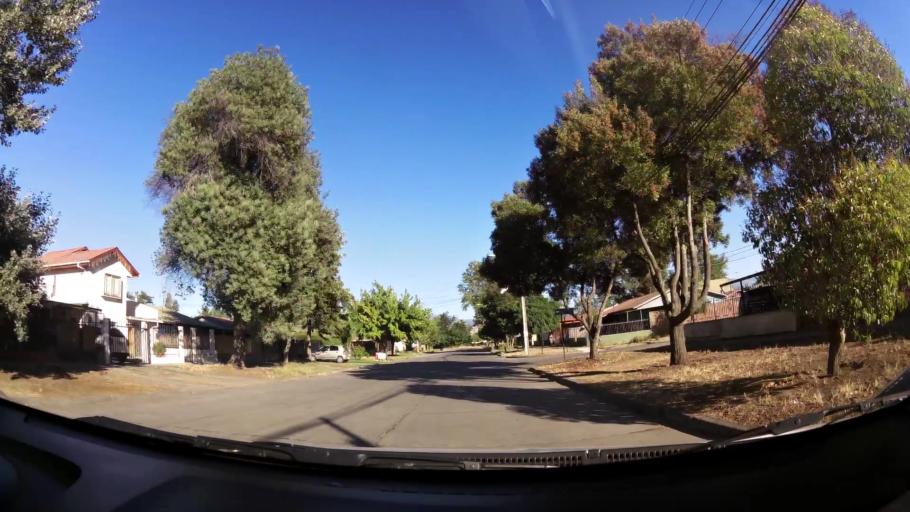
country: CL
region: O'Higgins
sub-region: Provincia de Cachapoal
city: Rancagua
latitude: -34.1751
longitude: -70.7232
